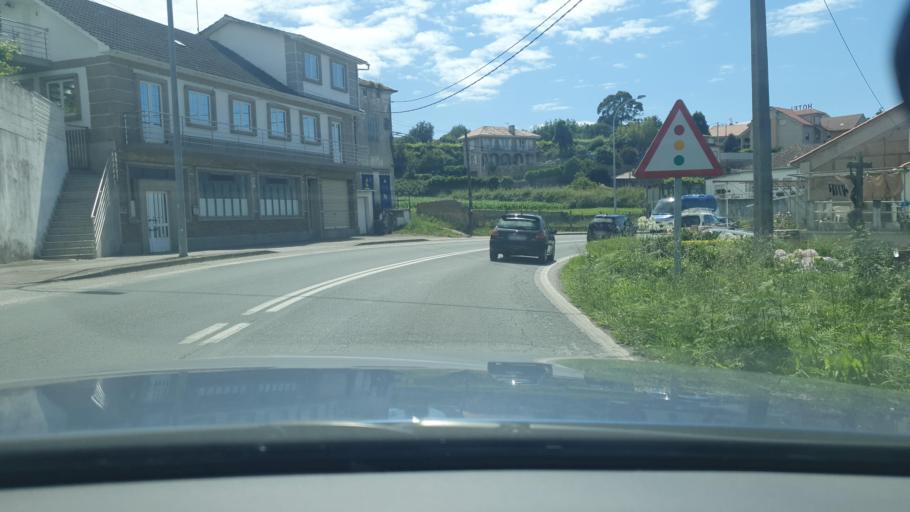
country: ES
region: Galicia
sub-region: Provincia de Pontevedra
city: Sanxenxo
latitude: 42.4403
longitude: -8.8428
